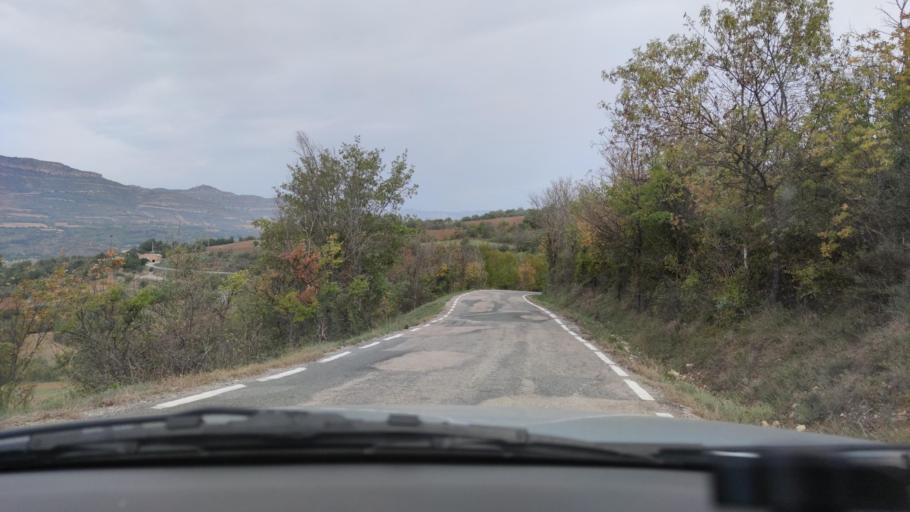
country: ES
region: Catalonia
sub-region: Provincia de Lleida
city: Llimiana
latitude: 42.0617
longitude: 0.9050
